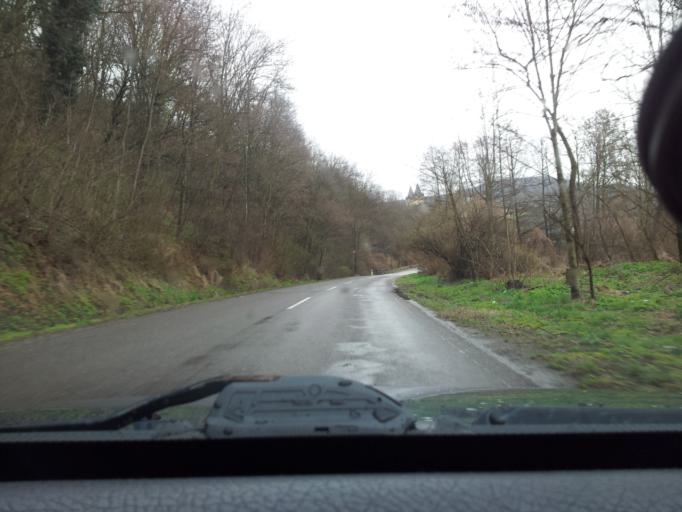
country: SK
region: Nitriansky
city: Tlmace
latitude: 48.3409
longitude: 18.5576
